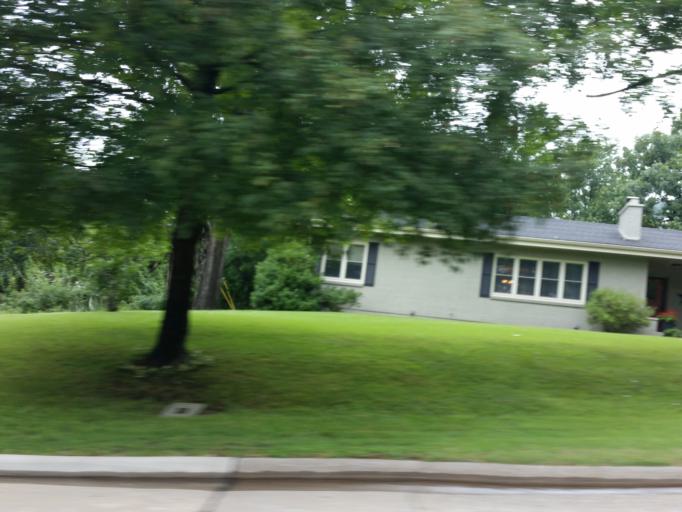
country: US
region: Missouri
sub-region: Cape Girardeau County
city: Cape Girardeau
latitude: 37.3278
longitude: -89.5475
